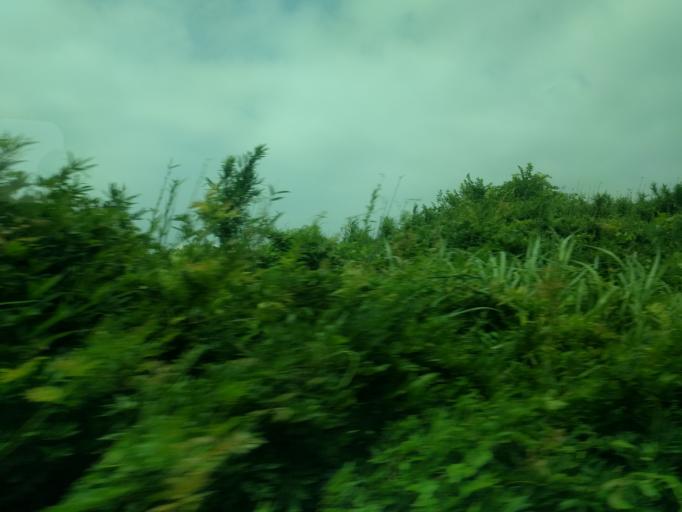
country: JP
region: Fukushima
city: Koriyama
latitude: 37.4658
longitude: 140.3273
